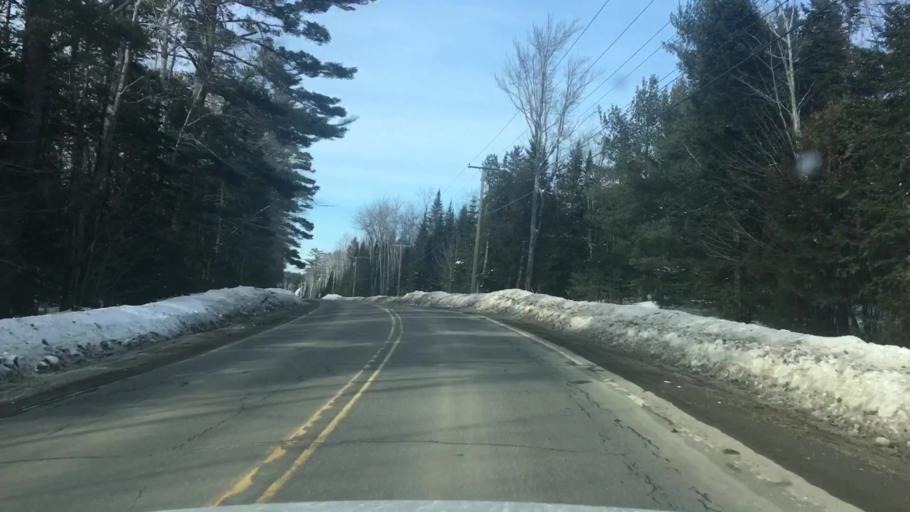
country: US
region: Maine
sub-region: Penobscot County
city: Charleston
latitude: 45.0460
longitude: -69.0289
